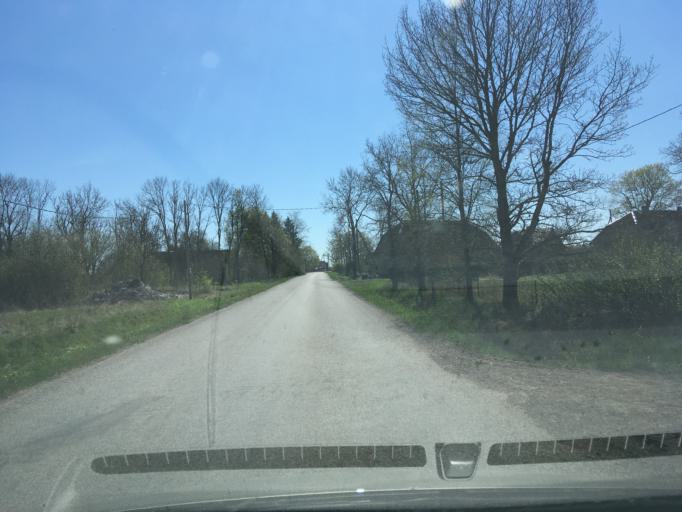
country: EE
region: Harju
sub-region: Raasiku vald
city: Arukula
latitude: 59.3920
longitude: 25.0799
